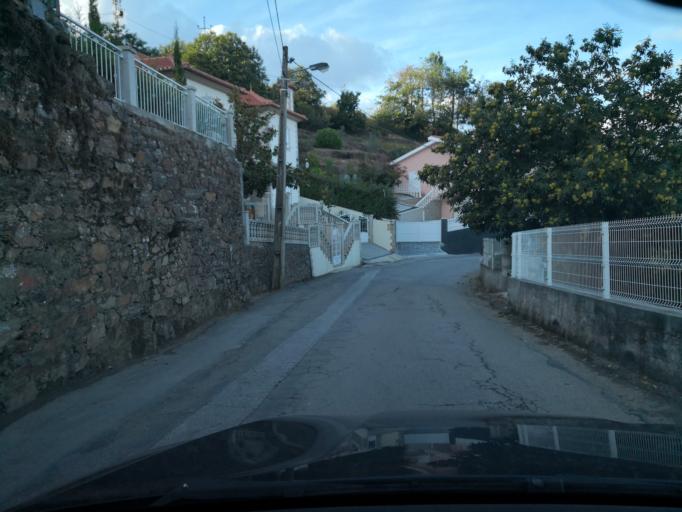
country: PT
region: Vila Real
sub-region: Santa Marta de Penaguiao
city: Santa Marta de Penaguiao
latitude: 41.2265
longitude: -7.8189
